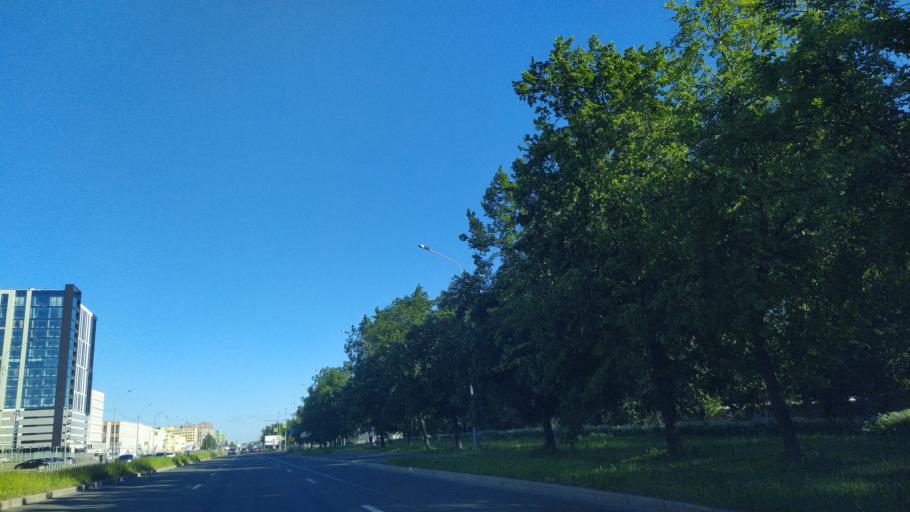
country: RU
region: St.-Petersburg
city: Kupchino
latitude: 59.8860
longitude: 30.3851
